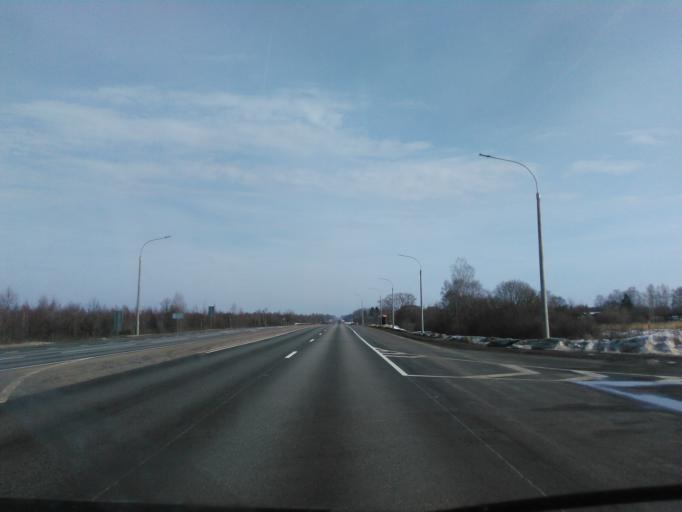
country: BY
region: Vitebsk
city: Dubrowna
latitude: 54.6893
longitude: 30.8892
